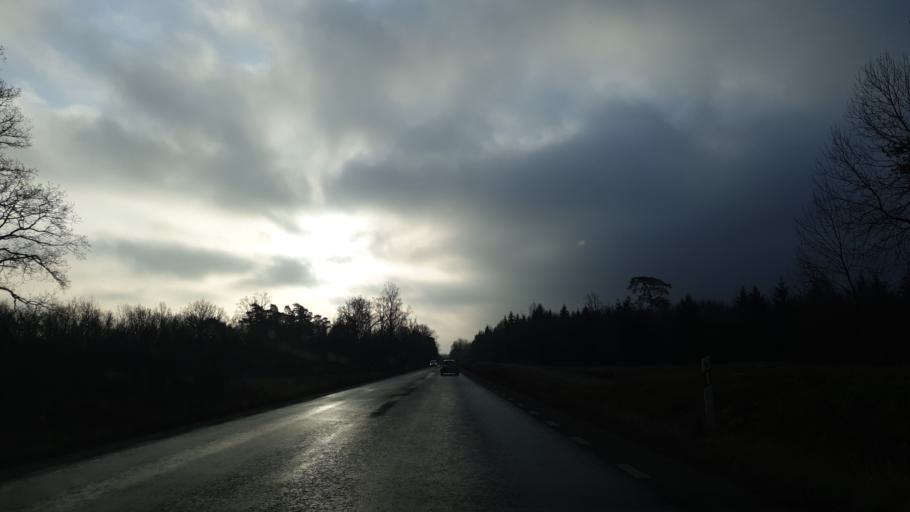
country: SE
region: Blekinge
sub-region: Karlshamns Kommun
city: Morrum
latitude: 56.1438
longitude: 14.6694
